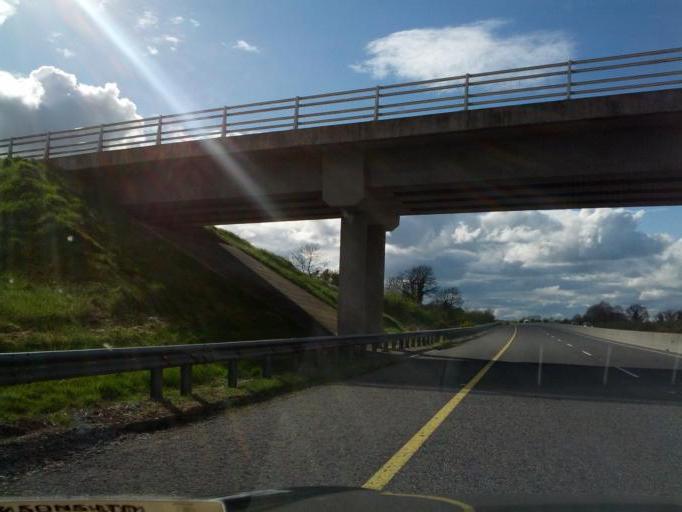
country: IE
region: Leinster
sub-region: Uibh Fhaili
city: Clara
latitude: 53.3795
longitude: -7.5651
